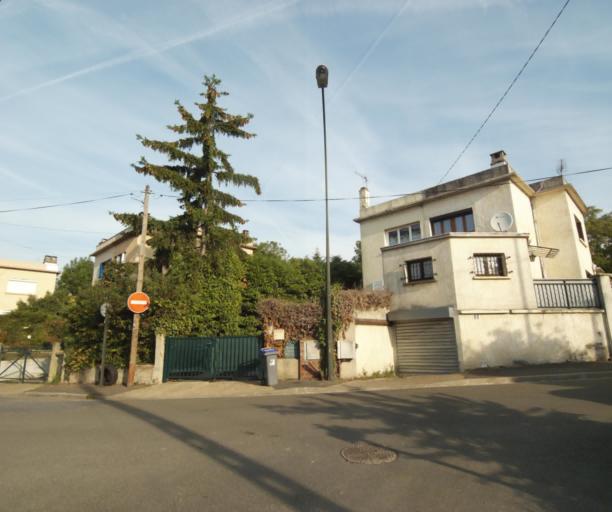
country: FR
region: Ile-de-France
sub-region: Departement du Val-d'Oise
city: Saint-Gratien
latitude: 48.9526
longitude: 2.2836
